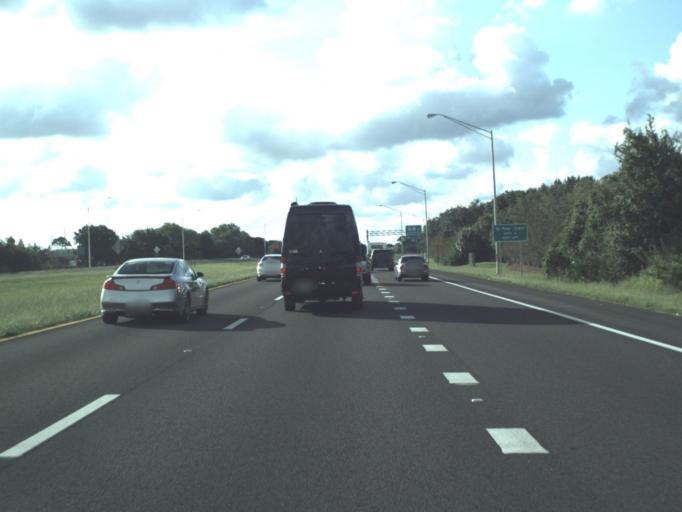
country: US
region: Florida
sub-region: Pinellas County
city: Feather Sound
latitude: 27.8874
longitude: -82.6702
